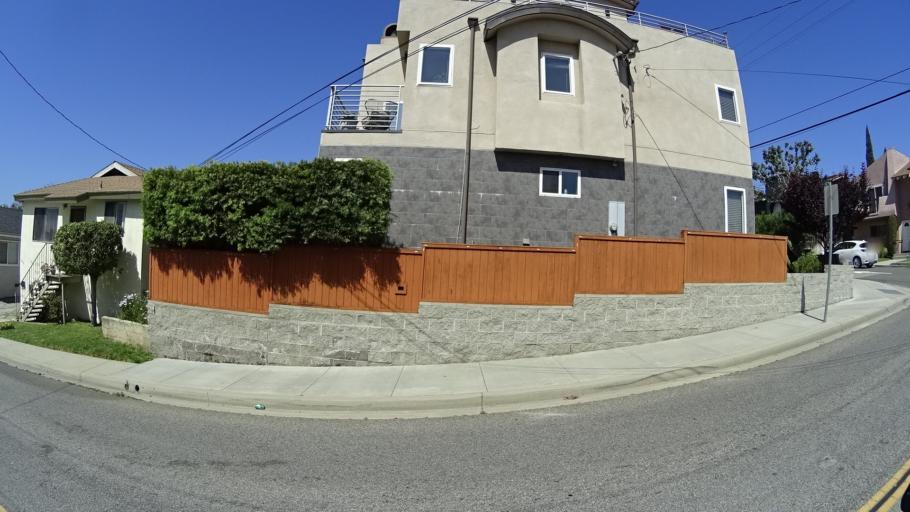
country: US
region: California
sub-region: Los Angeles County
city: Redondo Beach
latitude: 33.8669
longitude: -118.3727
